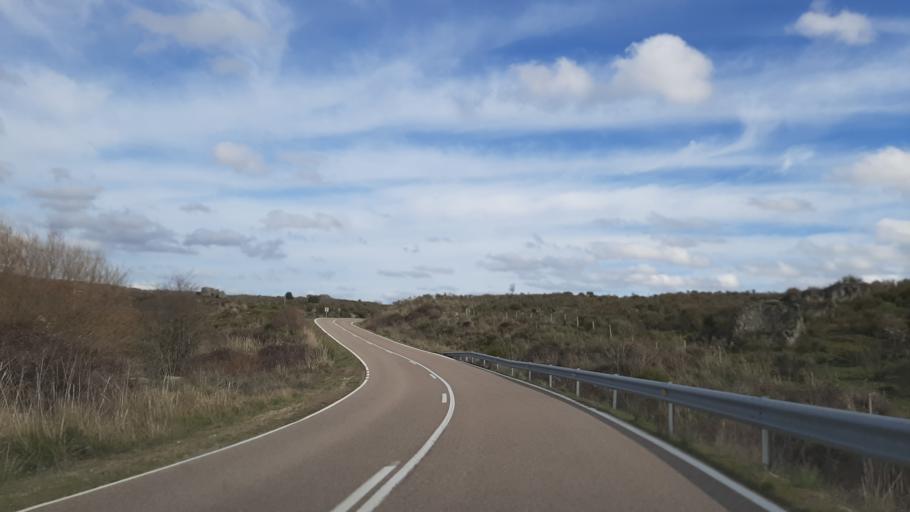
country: ES
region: Castille and Leon
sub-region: Provincia de Salamanca
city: Trabanca
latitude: 41.2569
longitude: -6.4204
